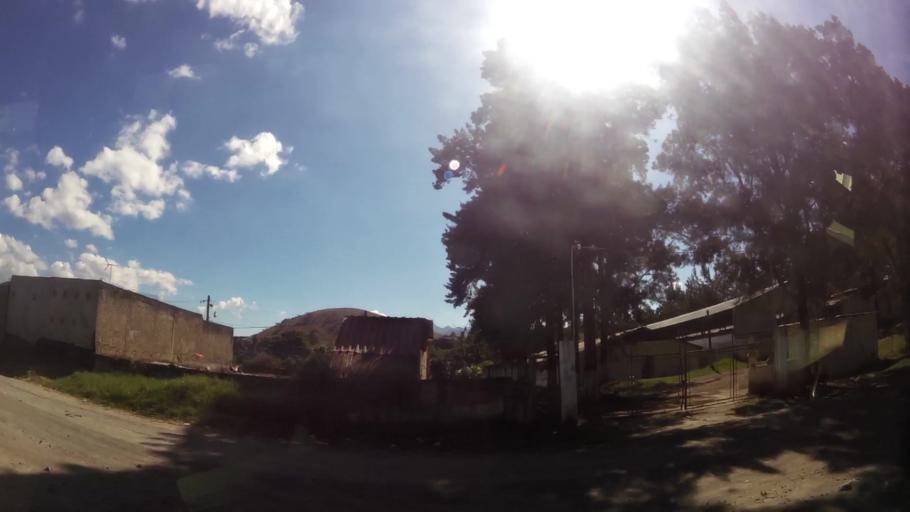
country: GT
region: Guatemala
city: Petapa
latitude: 14.4977
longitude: -90.5658
